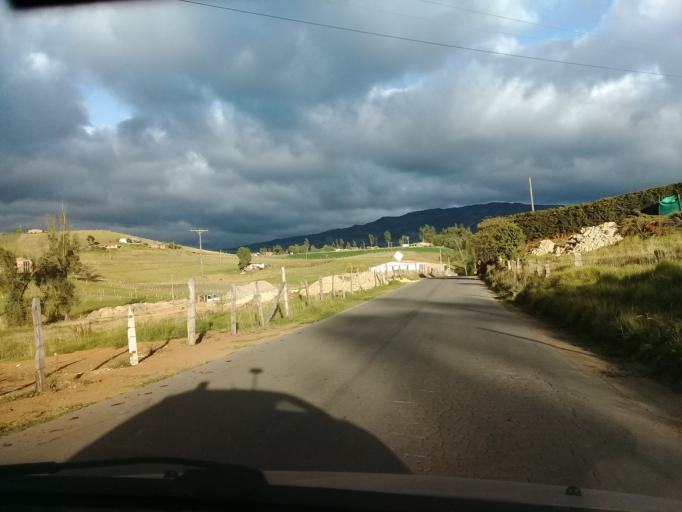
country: CO
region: Cundinamarca
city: Villapinzon
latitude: 5.2220
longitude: -73.6097
